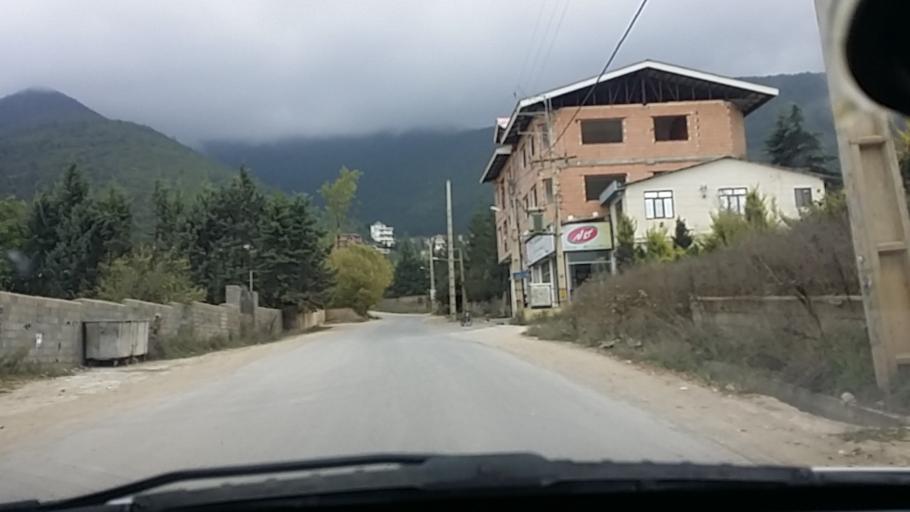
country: IR
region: Mazandaran
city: `Abbasabad
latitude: 36.4985
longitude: 51.1636
